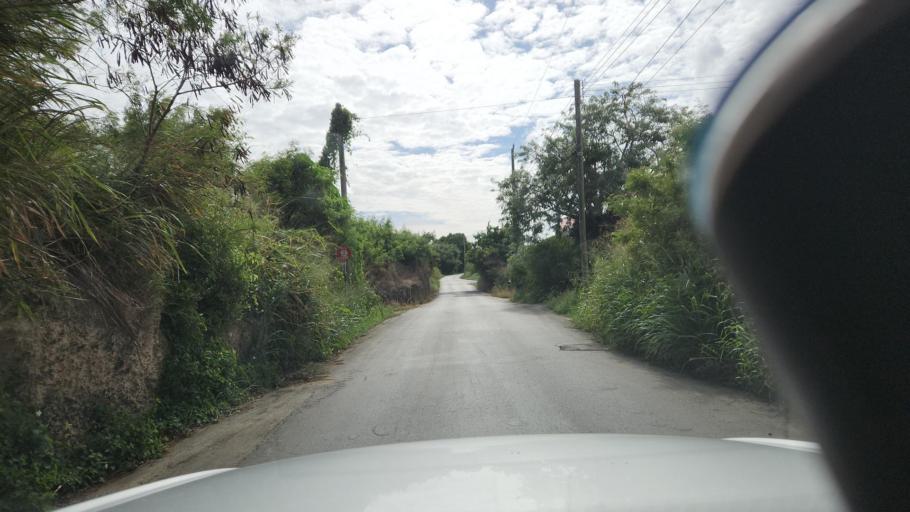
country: BB
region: Saint Lucy
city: Checker Hall
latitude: 13.2757
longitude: -59.6388
